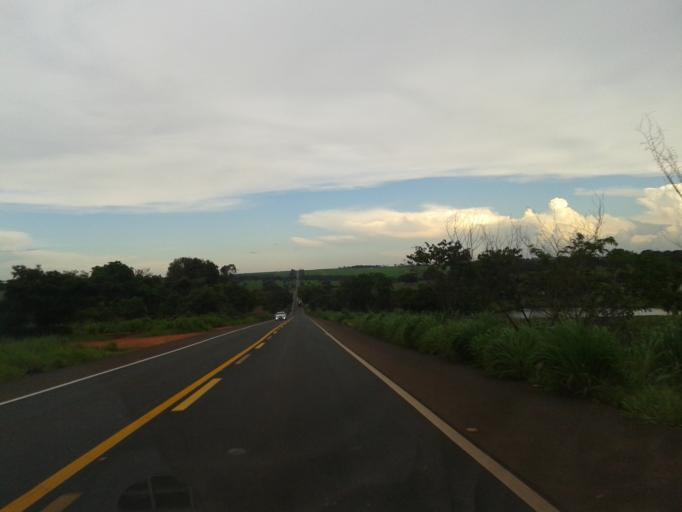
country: BR
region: Minas Gerais
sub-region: Santa Vitoria
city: Santa Vitoria
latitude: -18.9088
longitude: -50.2140
